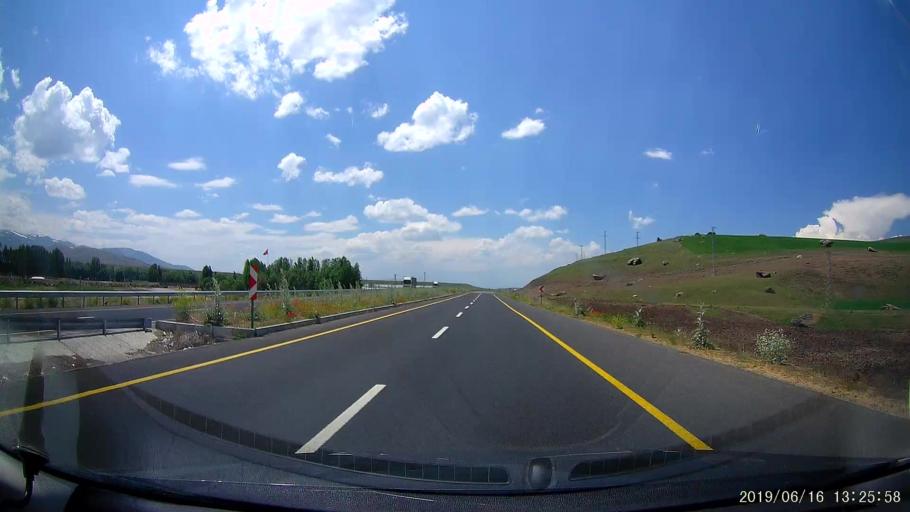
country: TR
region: Agri
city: Taslicay
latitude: 39.6566
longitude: 43.3397
